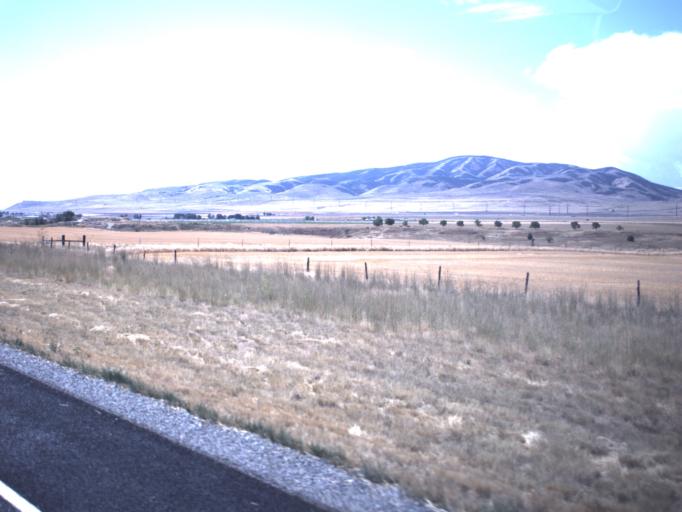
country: US
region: Utah
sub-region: Box Elder County
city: Garland
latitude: 41.8516
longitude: -112.1464
